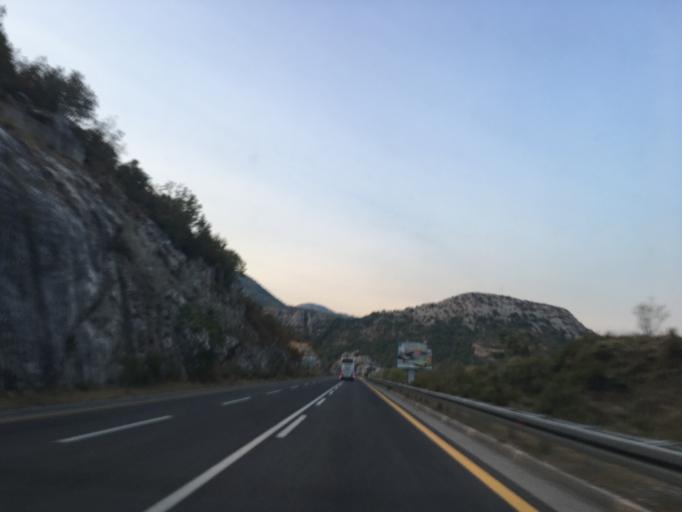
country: ME
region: Bar
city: Sutomore
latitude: 42.2158
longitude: 19.0495
